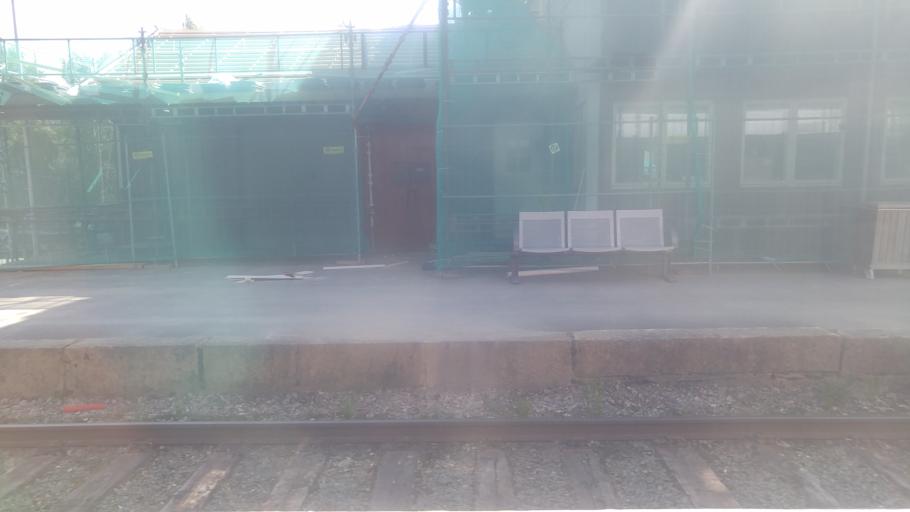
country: NO
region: Sor-Trondelag
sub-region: Holtalen
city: Alen
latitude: 62.9285
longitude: 11.1443
